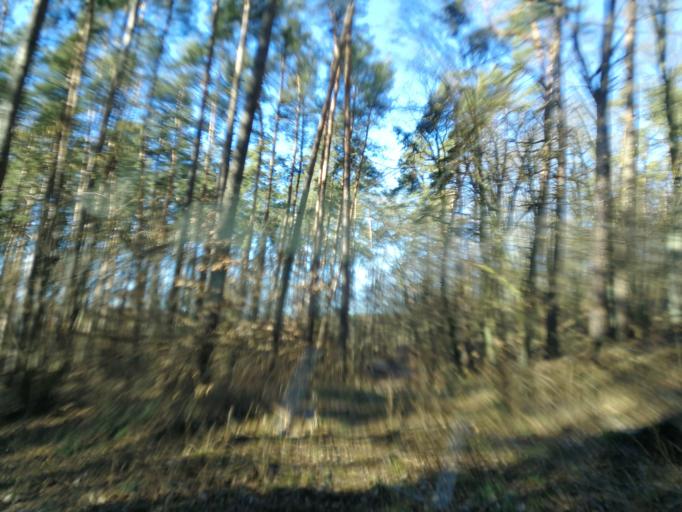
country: PL
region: Kujawsko-Pomorskie
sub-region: Powiat brodnicki
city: Gorzno
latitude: 53.2173
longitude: 19.6669
